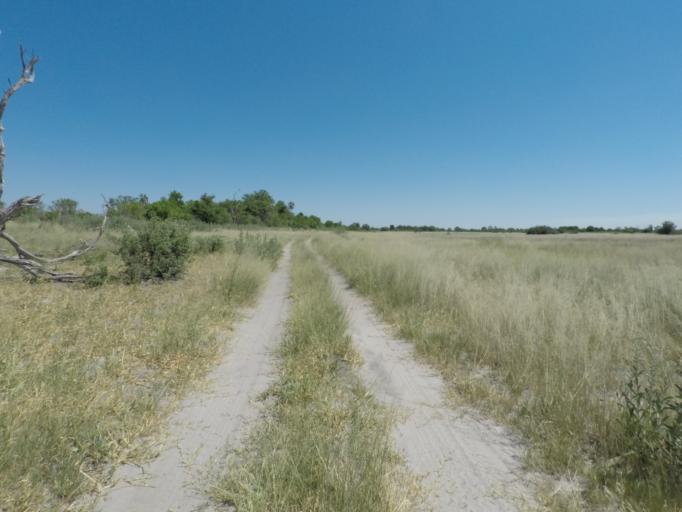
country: BW
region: North West
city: Maun
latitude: -19.4760
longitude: 23.5525
